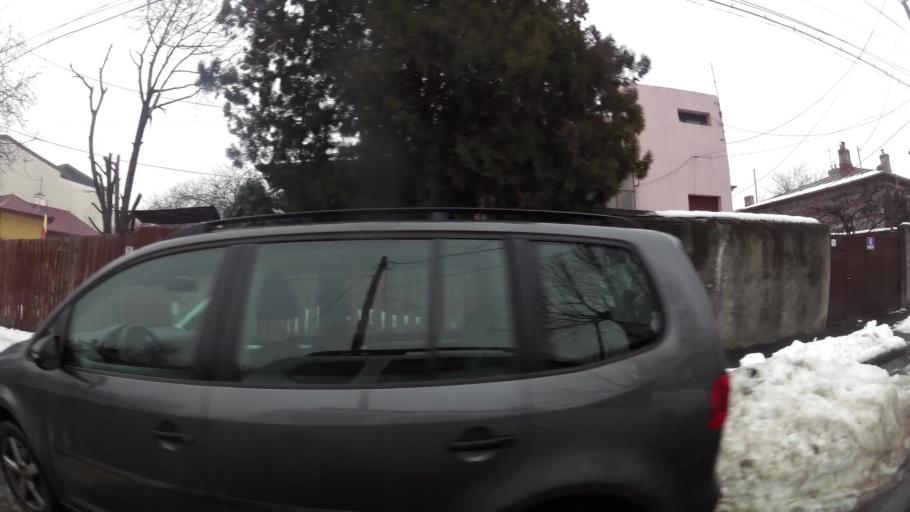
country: RO
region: Ilfov
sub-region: Comuna Chiajna
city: Rosu
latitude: 44.4685
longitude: 26.0322
